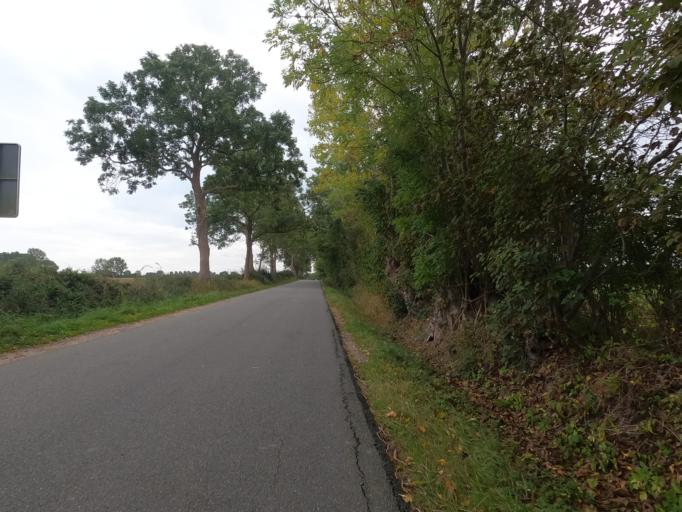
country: DE
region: Schleswig-Holstein
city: Neukirchen
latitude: 54.3173
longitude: 11.0378
